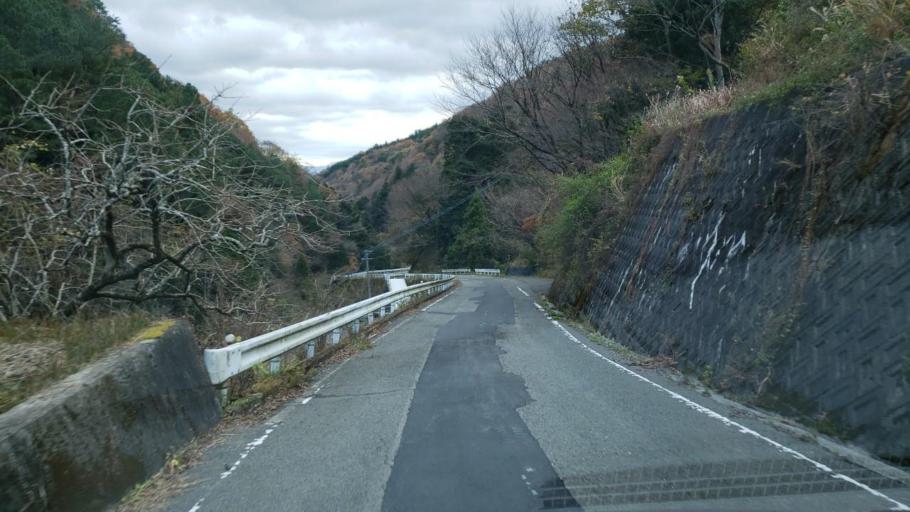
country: JP
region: Tokushima
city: Wakimachi
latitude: 34.1498
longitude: 134.2280
